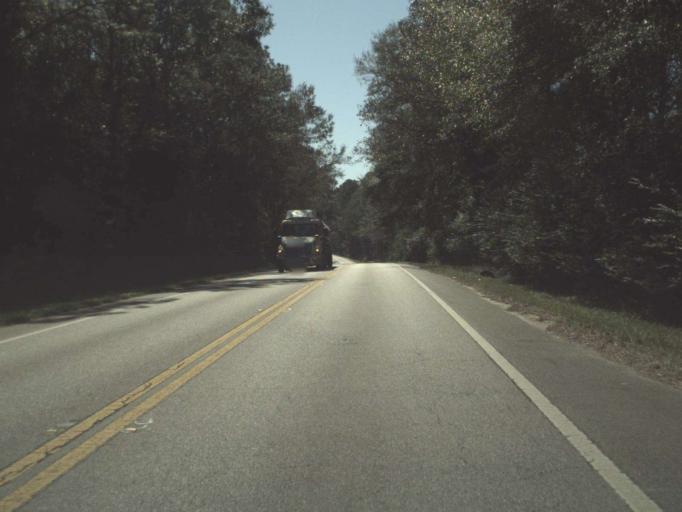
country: US
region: Florida
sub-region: Walton County
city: DeFuniak Springs
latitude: 30.9259
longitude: -86.1372
